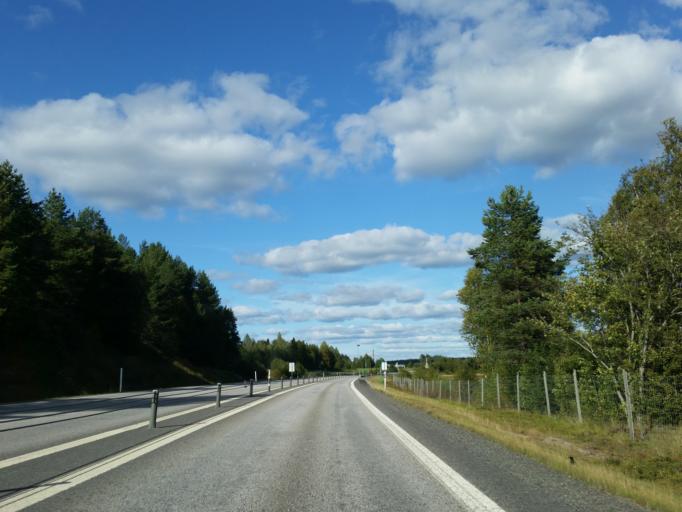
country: SE
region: Vaesterbotten
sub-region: Robertsfors Kommun
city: Robertsfors
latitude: 64.1593
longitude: 20.9160
